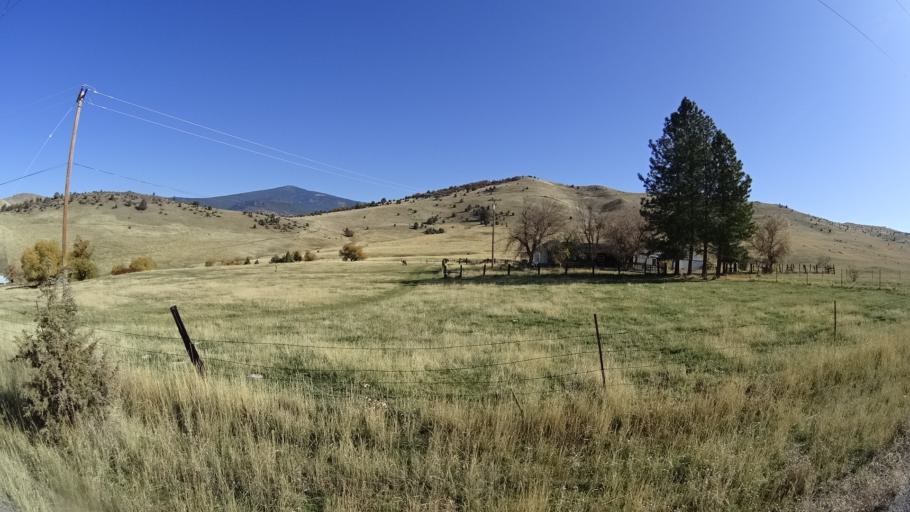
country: US
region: California
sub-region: Siskiyou County
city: Montague
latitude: 41.7843
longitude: -122.3590
